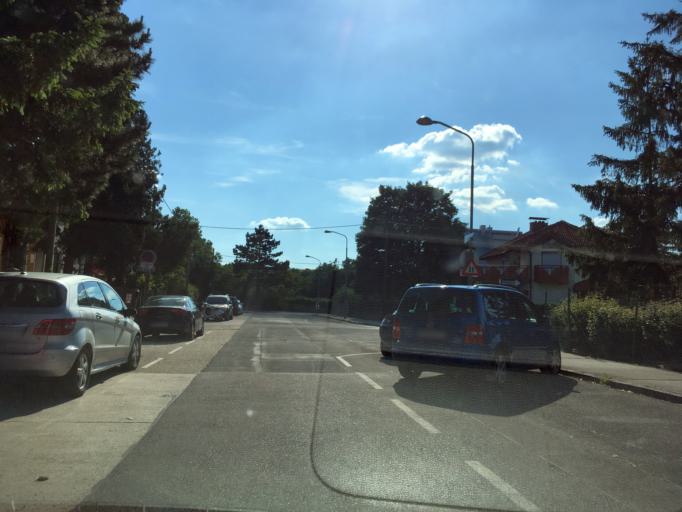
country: AT
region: Lower Austria
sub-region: Politischer Bezirk Korneuburg
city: Langenzersdorf
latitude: 48.2739
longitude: 16.3863
